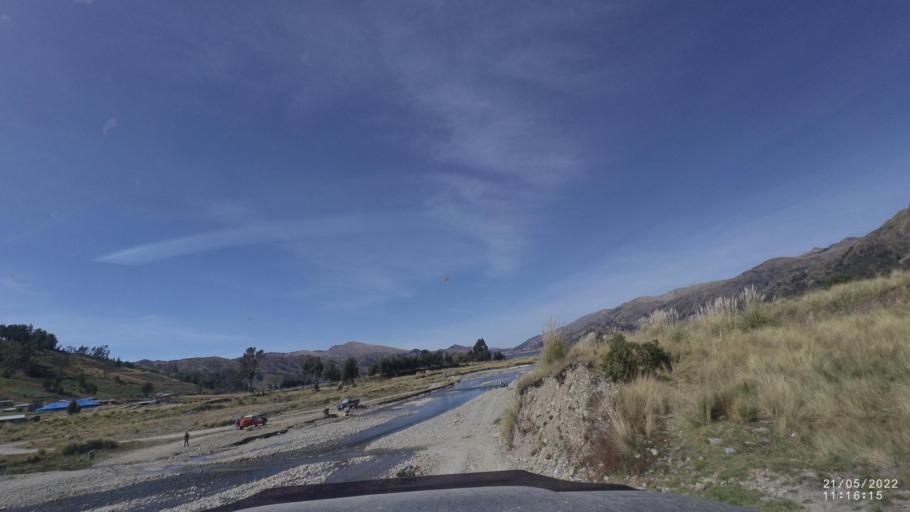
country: BO
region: Cochabamba
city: Colomi
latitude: -17.2762
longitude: -65.9222
